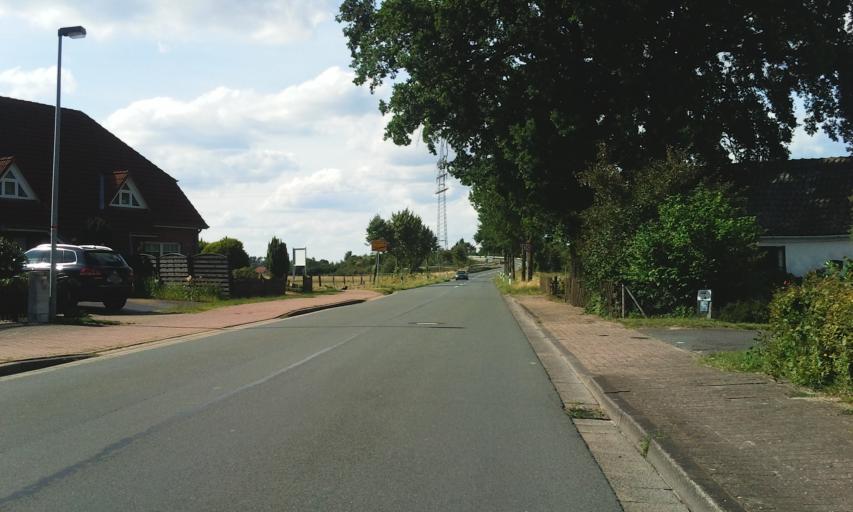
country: DE
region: Lower Saxony
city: Drakenburg
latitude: 52.6787
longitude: 9.2247
